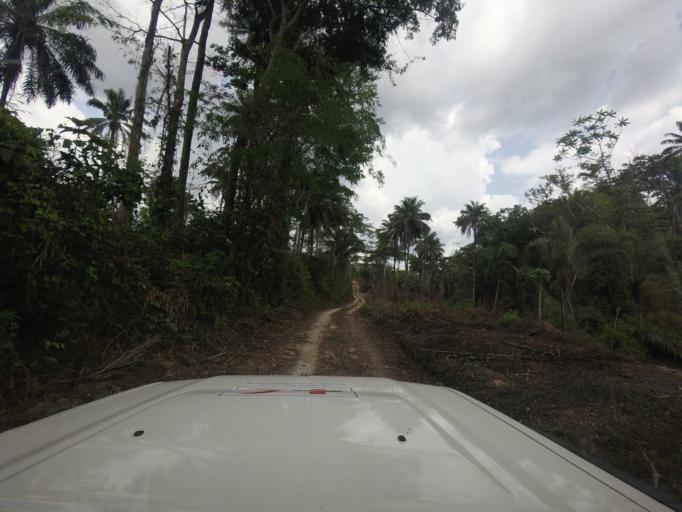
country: LR
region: Lofa
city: Voinjama
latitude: 8.3919
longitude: -9.6219
